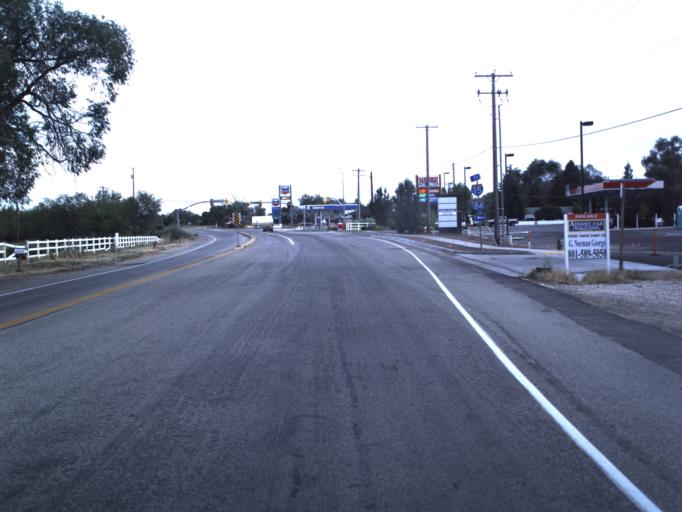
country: US
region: Utah
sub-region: Weber County
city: Marriott-Slaterville
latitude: 41.2705
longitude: -112.0283
